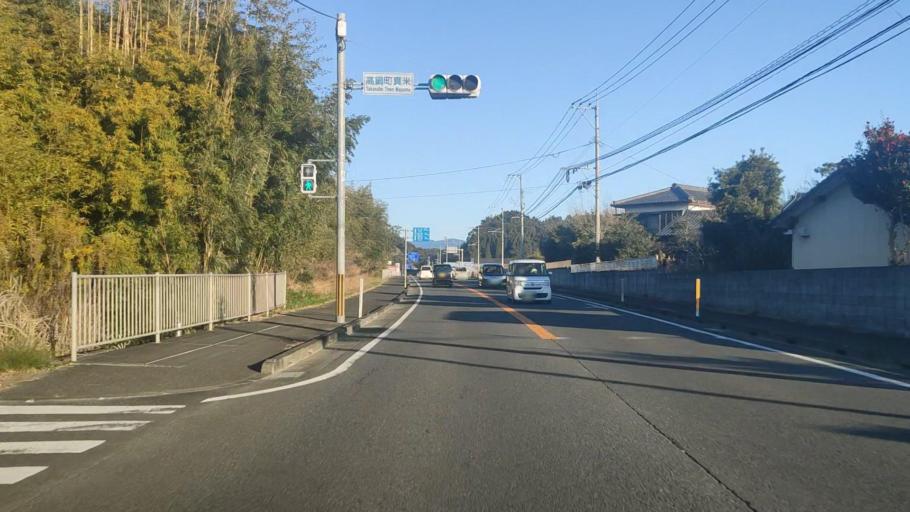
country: JP
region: Miyazaki
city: Takanabe
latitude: 32.1402
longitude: 131.5276
